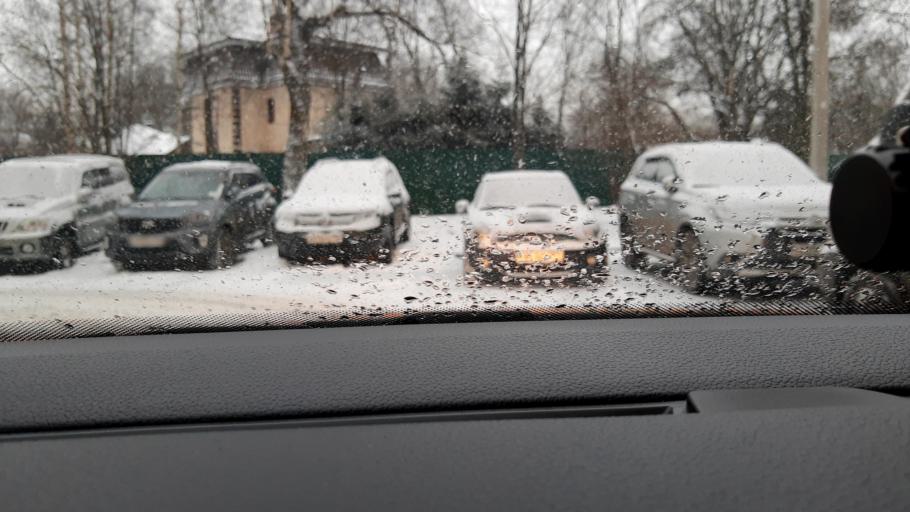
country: RU
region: Moskovskaya
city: Skhodnya
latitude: 55.9461
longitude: 37.2918
